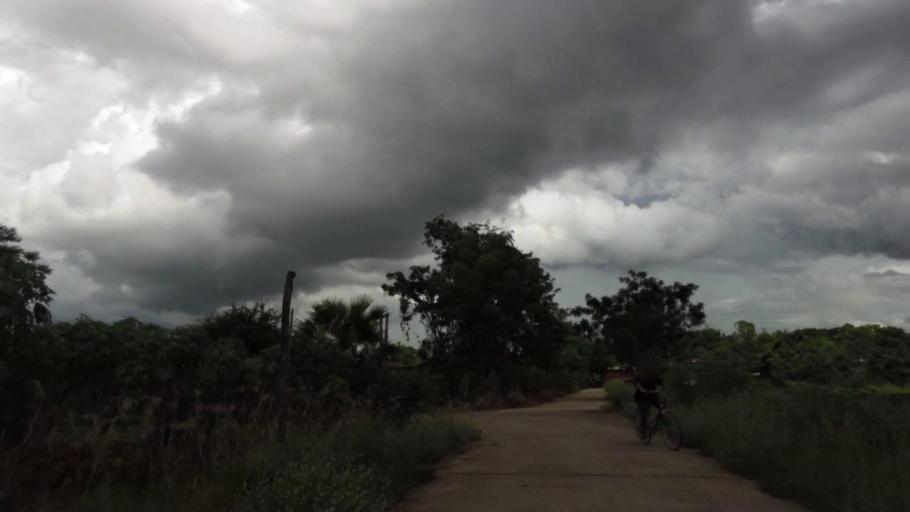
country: TH
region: Nakhon Sawan
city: Phai Sali
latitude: 15.6069
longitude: 100.6540
